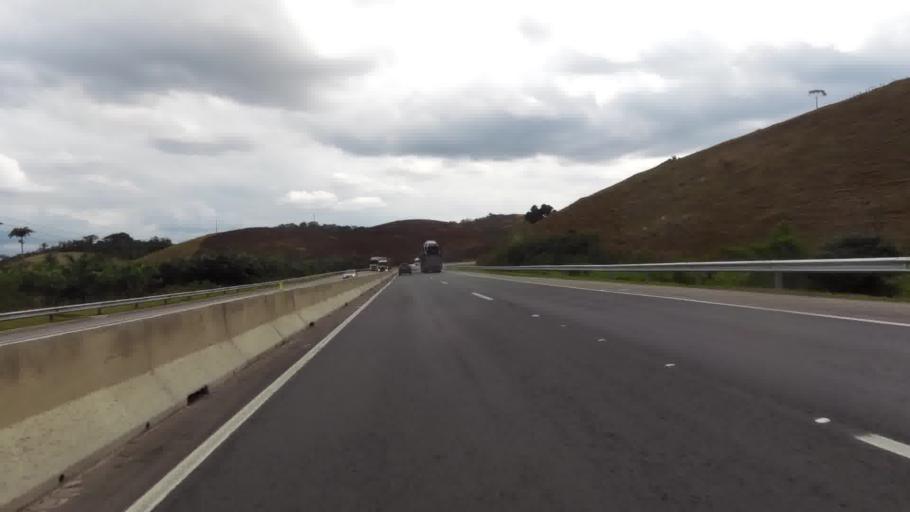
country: BR
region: Rio de Janeiro
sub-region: Casimiro De Abreu
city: Casimiro de Abreu
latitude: -22.4715
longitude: -42.0791
